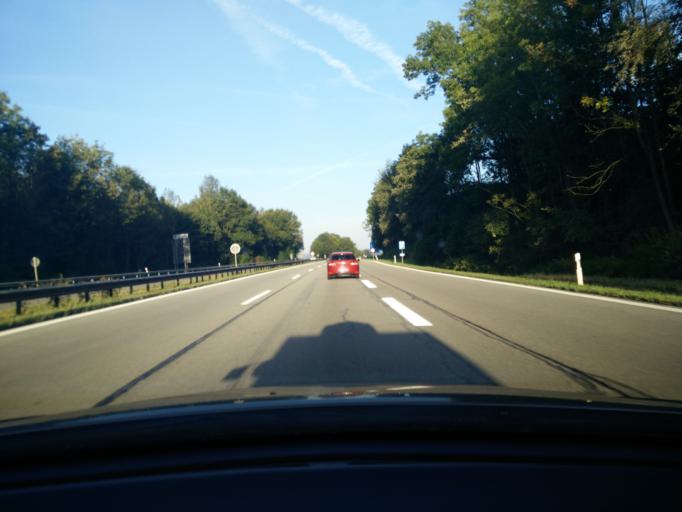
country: DE
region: Bavaria
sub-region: Upper Bavaria
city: Rohrdorf
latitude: 47.8026
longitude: 12.1726
